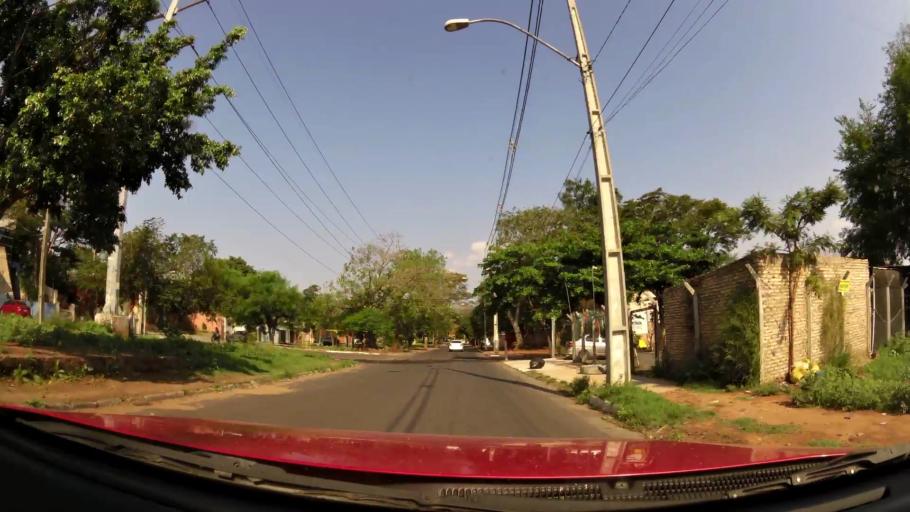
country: PY
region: Asuncion
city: Asuncion
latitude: -25.3127
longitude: -57.6345
